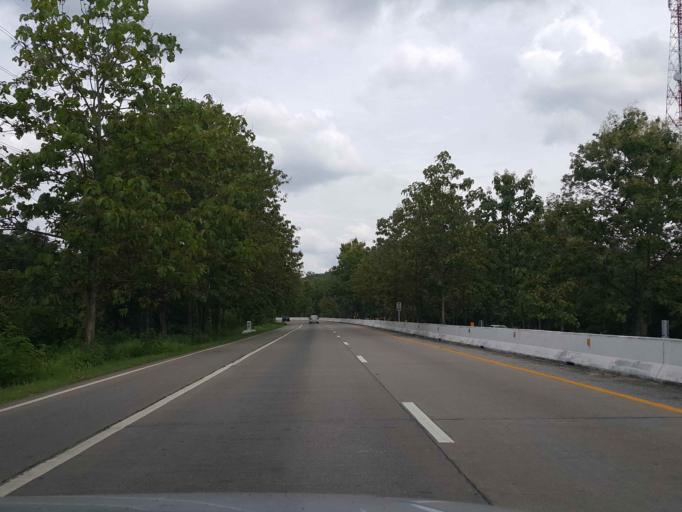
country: TH
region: Lamphun
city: Mae Tha
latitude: 18.5110
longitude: 99.0970
